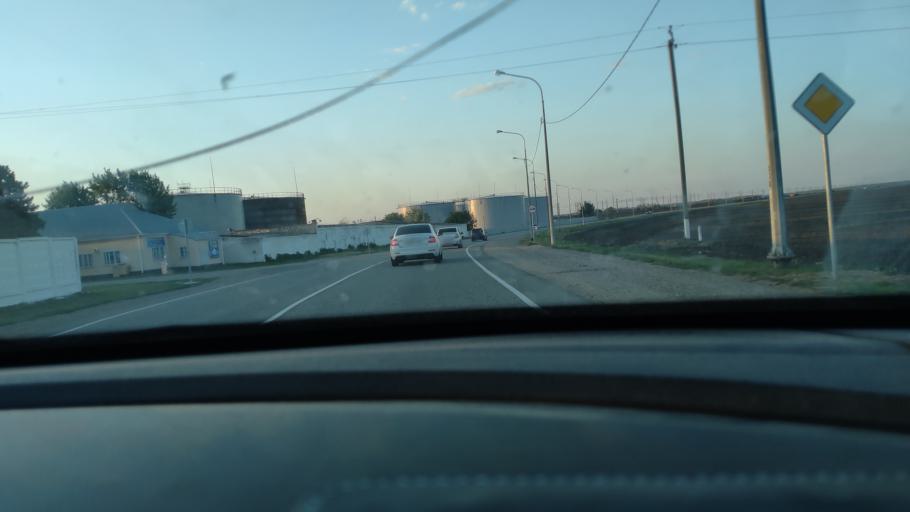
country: RU
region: Krasnodarskiy
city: Novominskaya
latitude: 46.3295
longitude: 38.9459
